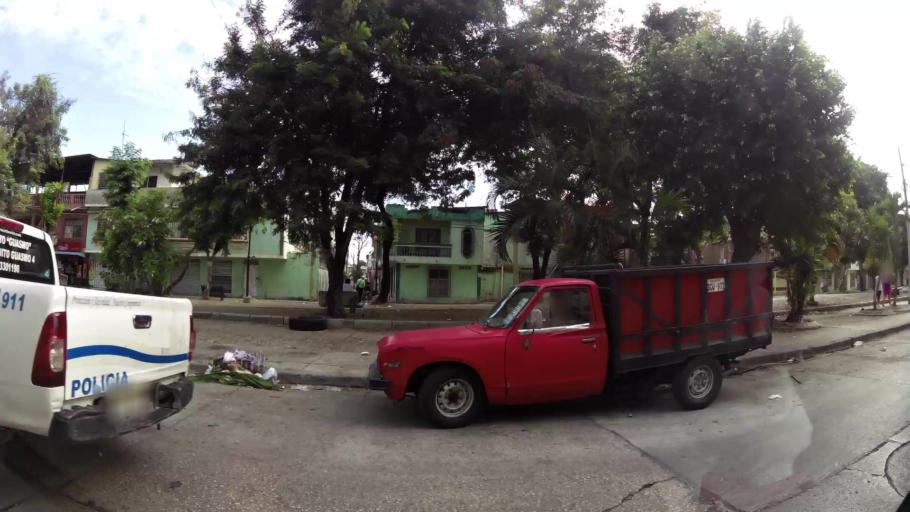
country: EC
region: Guayas
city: Guayaquil
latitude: -2.2504
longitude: -79.8871
